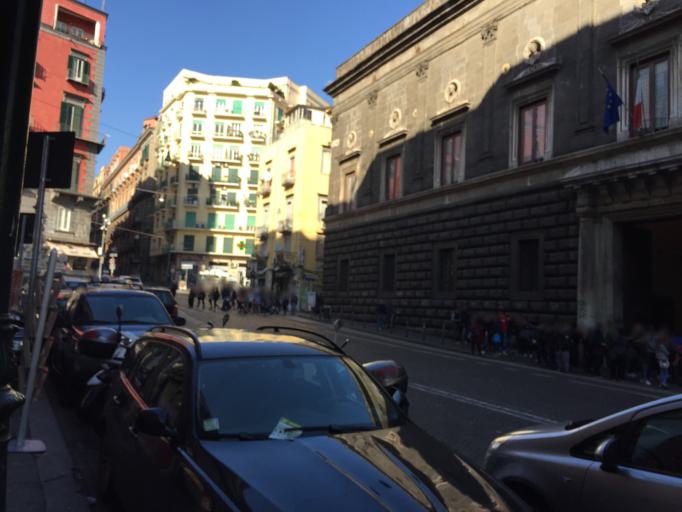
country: IT
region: Campania
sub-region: Provincia di Napoli
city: Napoli
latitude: 40.8449
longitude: 14.2513
